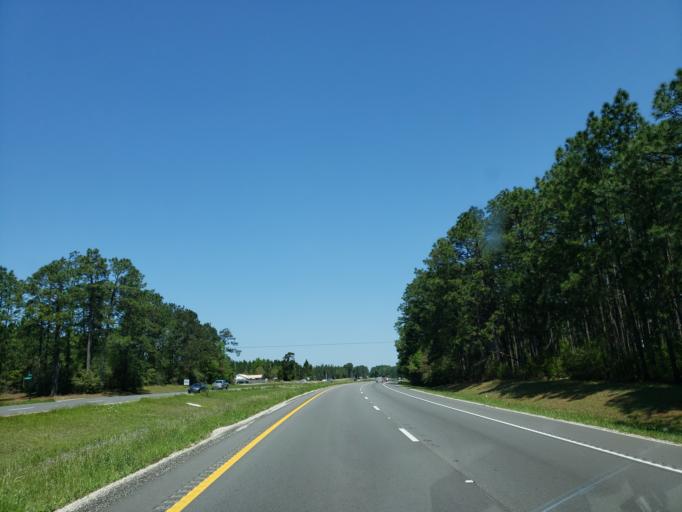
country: US
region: Mississippi
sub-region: Stone County
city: Wiggins
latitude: 30.8692
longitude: -89.1653
